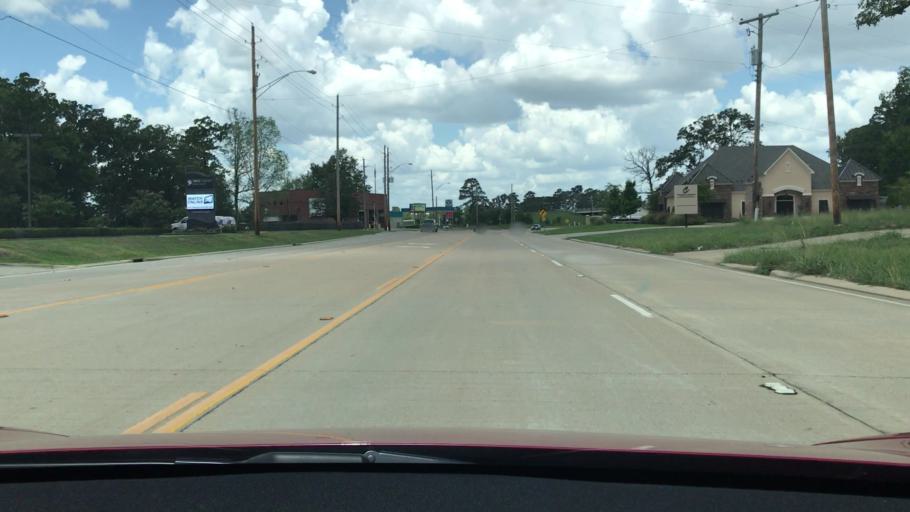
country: US
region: Louisiana
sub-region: Bossier Parish
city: Bossier City
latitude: 32.3982
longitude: -93.7319
